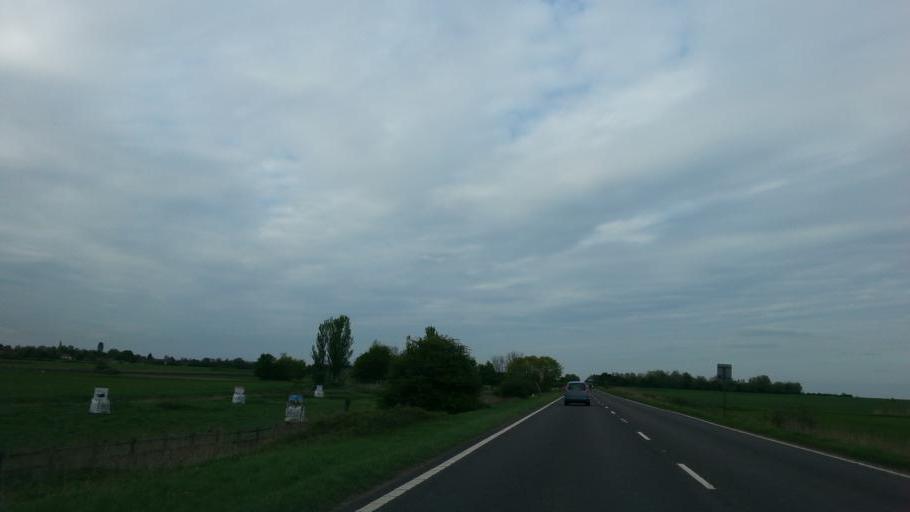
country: GB
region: England
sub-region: Cambridgeshire
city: Doddington
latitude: 52.4841
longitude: 0.0623
